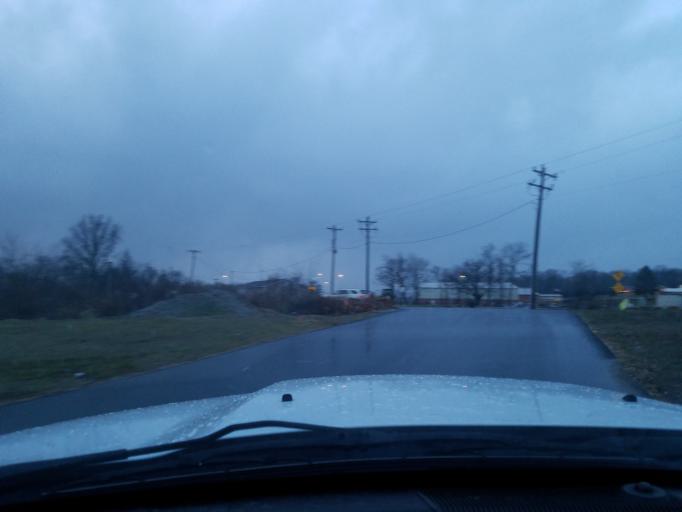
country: US
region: Indiana
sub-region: Clark County
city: Oak Park
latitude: 38.3367
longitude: -85.7061
